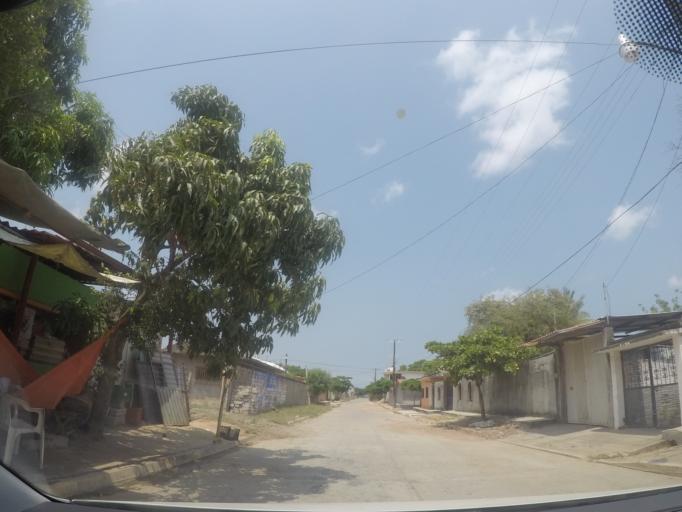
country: MX
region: Oaxaca
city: Asuncion Ixtaltepec
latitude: 16.5000
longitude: -95.0633
